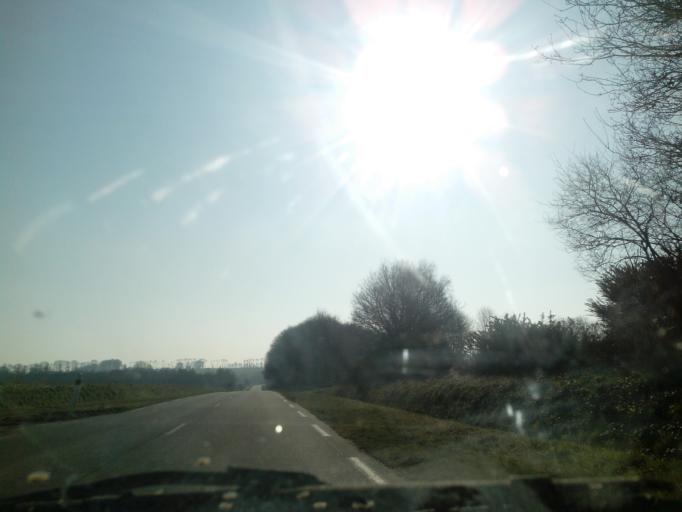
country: FR
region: Brittany
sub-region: Departement des Cotes-d'Armor
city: Merdrignac
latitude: 48.1794
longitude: -2.4307
